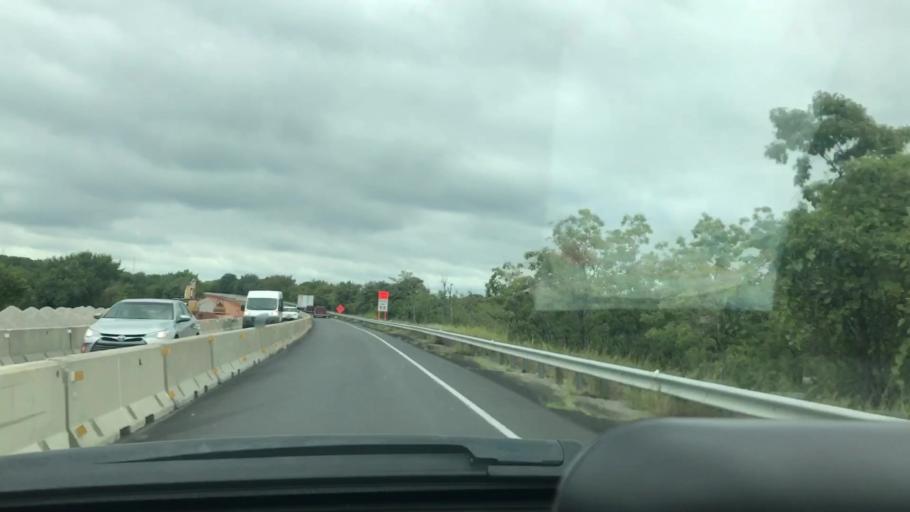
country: US
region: Oklahoma
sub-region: McIntosh County
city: Eufaula
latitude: 35.2481
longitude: -95.5850
